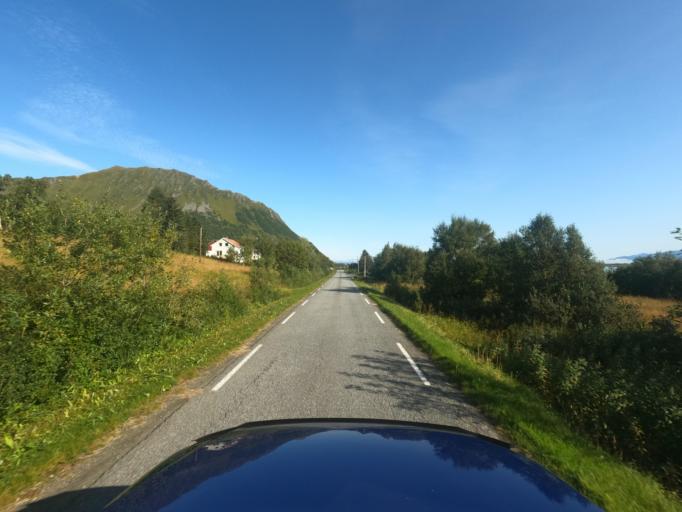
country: NO
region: Nordland
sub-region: Vestvagoy
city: Evjen
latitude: 68.2884
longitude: 13.9975
